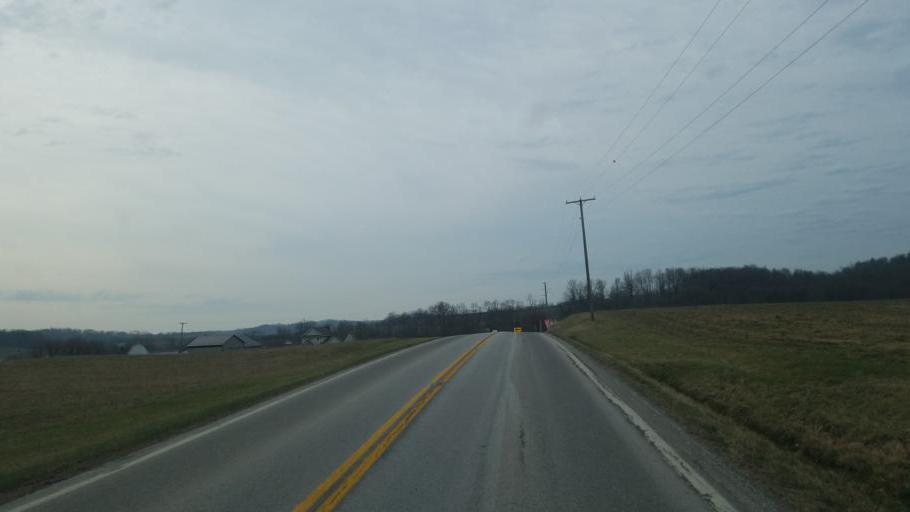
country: US
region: Ohio
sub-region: Holmes County
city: Millersburg
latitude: 40.5370
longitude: -81.8170
